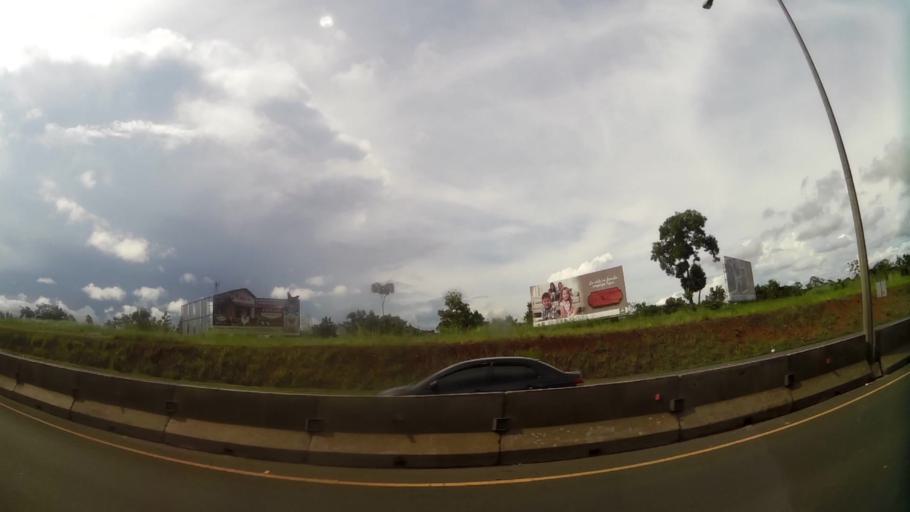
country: PA
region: Panama
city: La Chorrera
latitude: 8.8848
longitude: -79.7558
